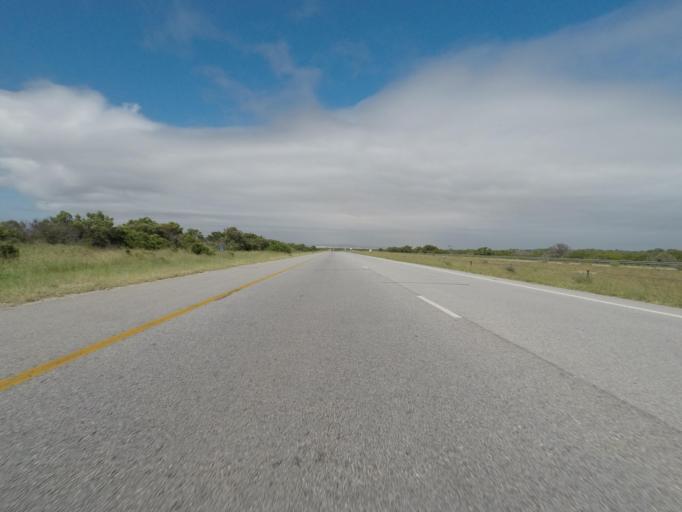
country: ZA
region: Eastern Cape
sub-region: Nelson Mandela Bay Metropolitan Municipality
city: Port Elizabeth
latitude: -33.7328
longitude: 25.7546
